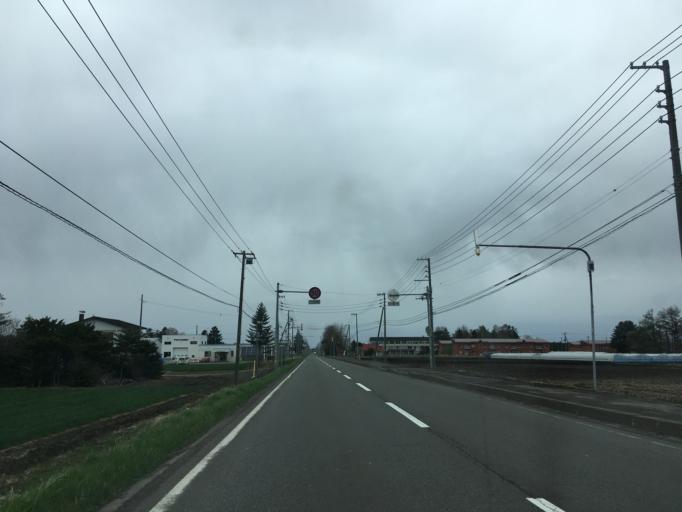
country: JP
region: Hokkaido
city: Chitose
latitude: 42.9379
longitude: 141.8053
